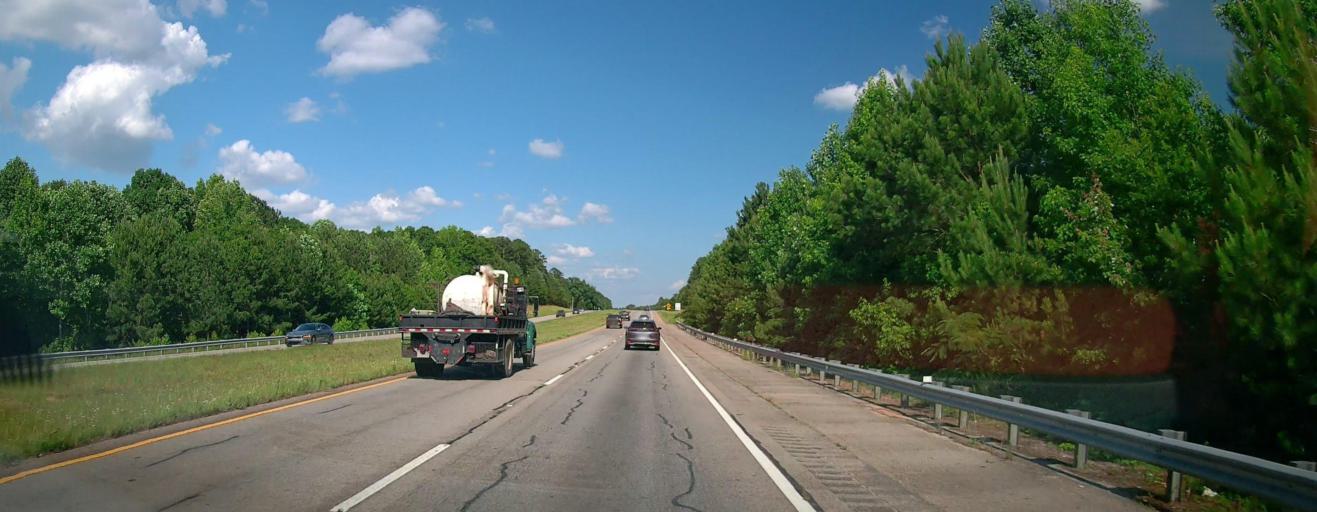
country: US
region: Georgia
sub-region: Henry County
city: Hampton
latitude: 33.3787
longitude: -84.2828
